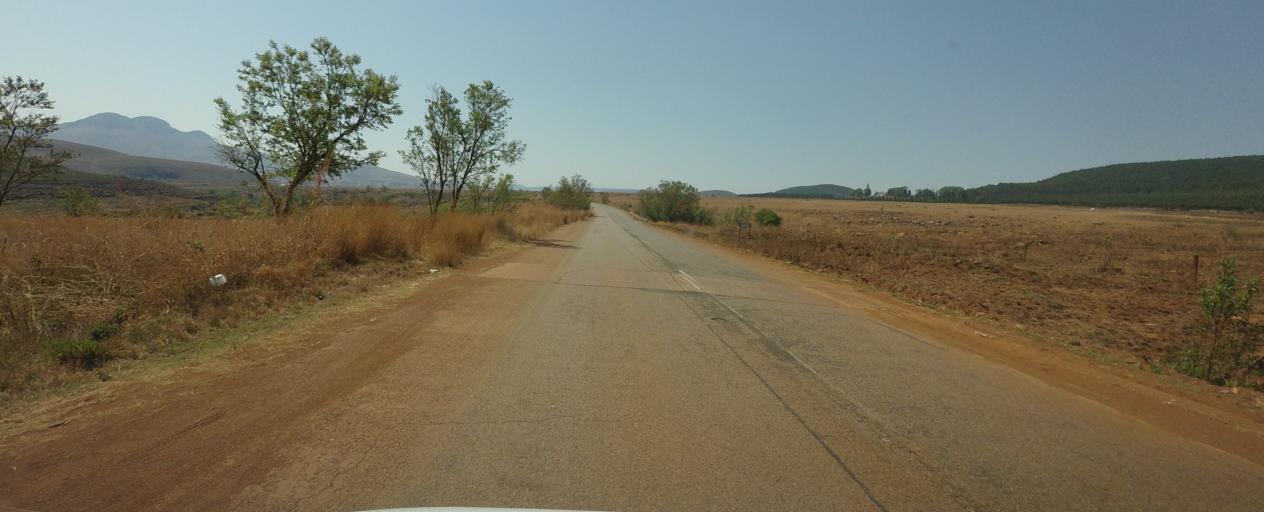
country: ZA
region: Mpumalanga
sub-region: Ehlanzeni District
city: Graksop
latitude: -24.7025
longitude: 30.8196
